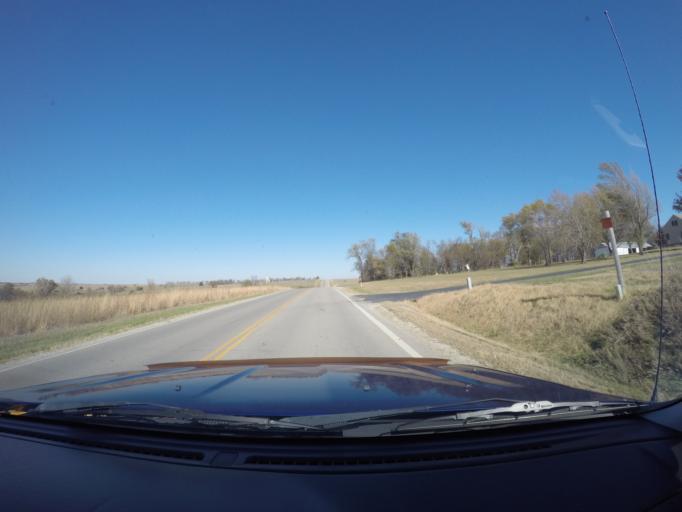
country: US
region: Kansas
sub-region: Marshall County
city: Marysville
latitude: 39.8460
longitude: -96.4169
